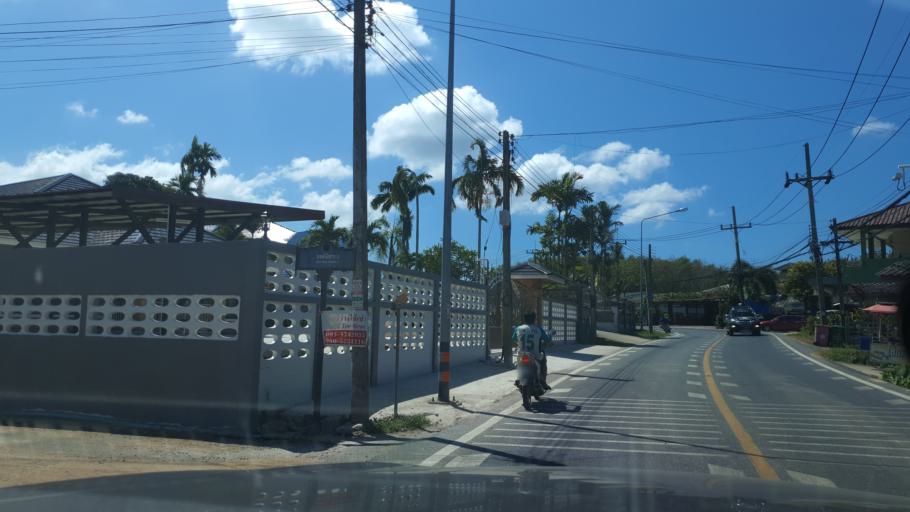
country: TH
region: Phuket
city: Thalang
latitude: 8.1242
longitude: 98.3120
